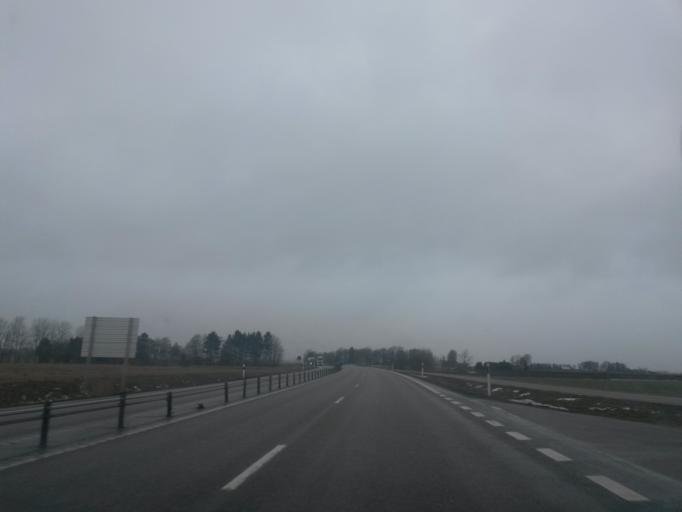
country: SE
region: Vaestra Goetaland
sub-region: Vanersborgs Kommun
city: Vargon
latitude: 58.2921
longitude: 12.3907
